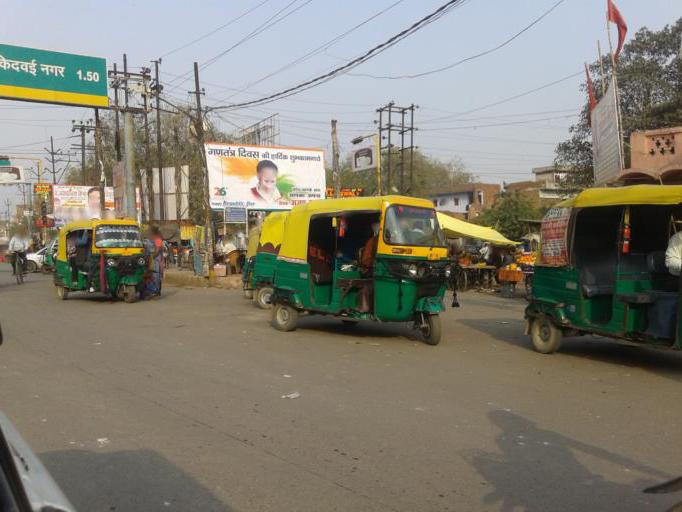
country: IN
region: Uttar Pradesh
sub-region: Kanpur
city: Kanpur
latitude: 26.4391
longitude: 80.3251
